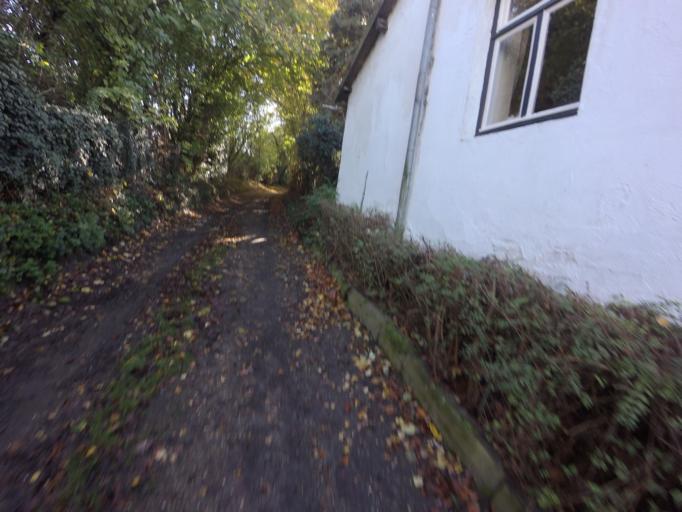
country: NL
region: Limburg
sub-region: Eijsden-Margraten
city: Margraten
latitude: 50.7981
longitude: 5.8687
